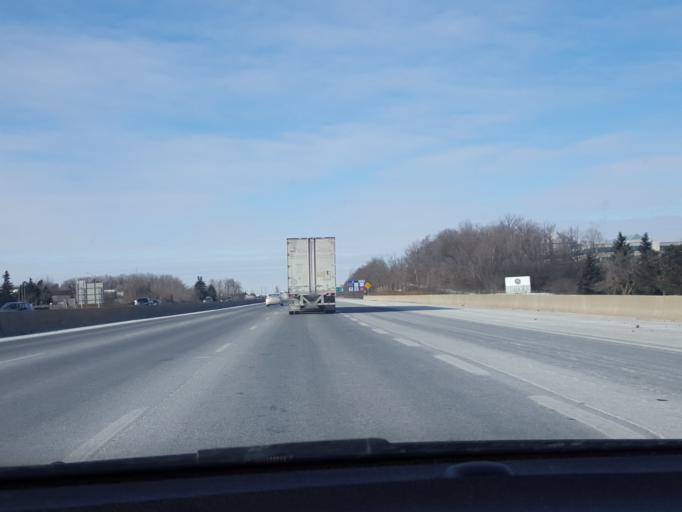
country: CA
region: Ontario
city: Brampton
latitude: 43.6029
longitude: -79.7562
